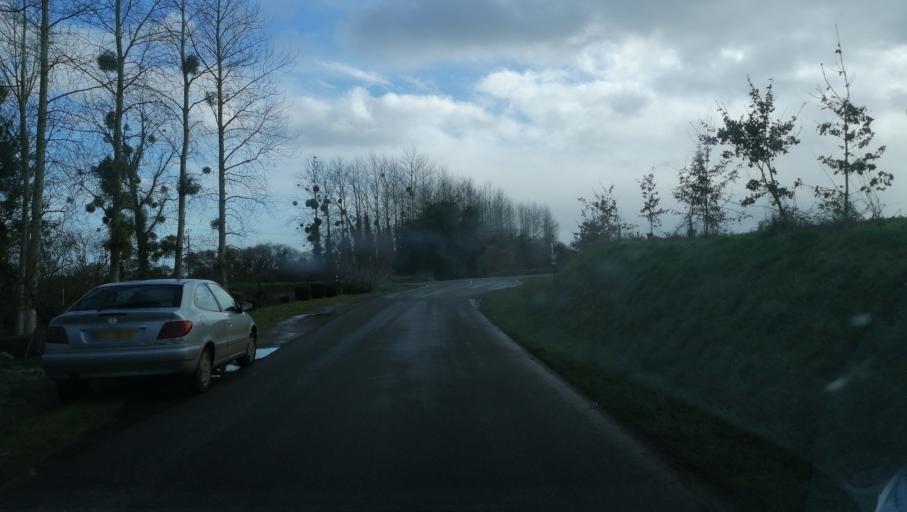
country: FR
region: Brittany
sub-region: Departement des Cotes-d'Armor
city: Lantic
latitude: 48.5890
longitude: -2.9149
